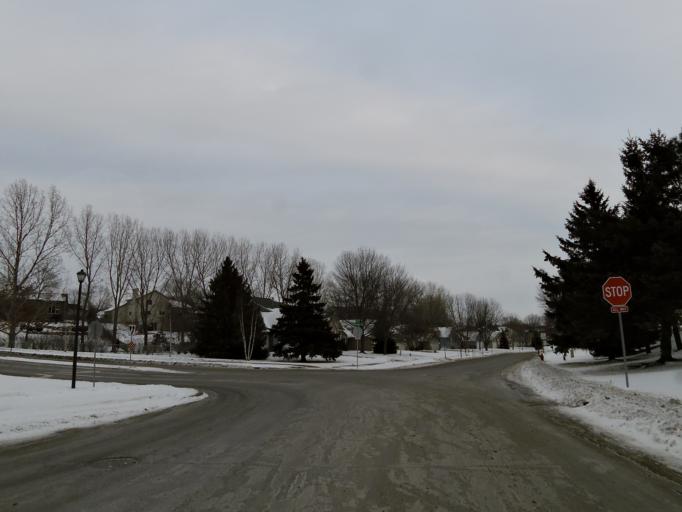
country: US
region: Minnesota
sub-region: Washington County
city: Woodbury
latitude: 44.9149
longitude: -92.9175
